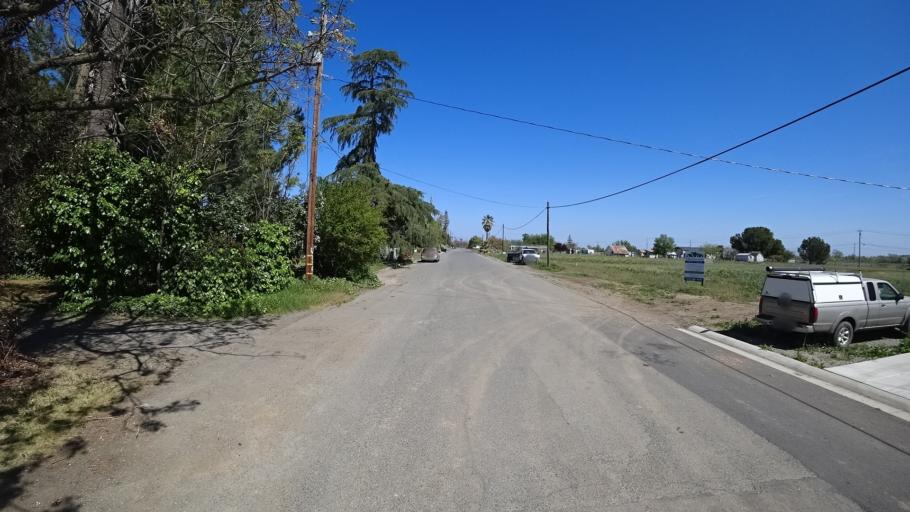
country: US
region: California
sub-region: Glenn County
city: Willows
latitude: 39.5277
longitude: -122.1867
